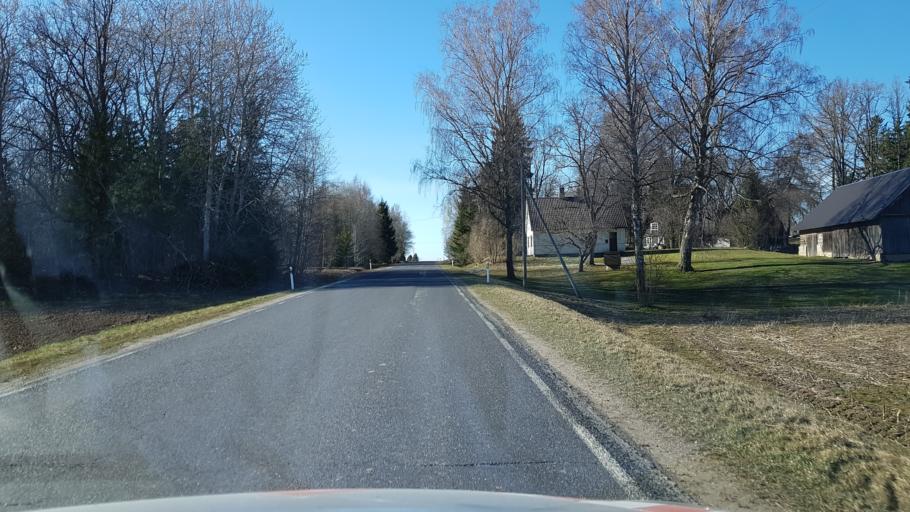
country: EE
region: Laeaene-Virumaa
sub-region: Vinni vald
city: Vinni
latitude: 59.3184
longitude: 26.5099
